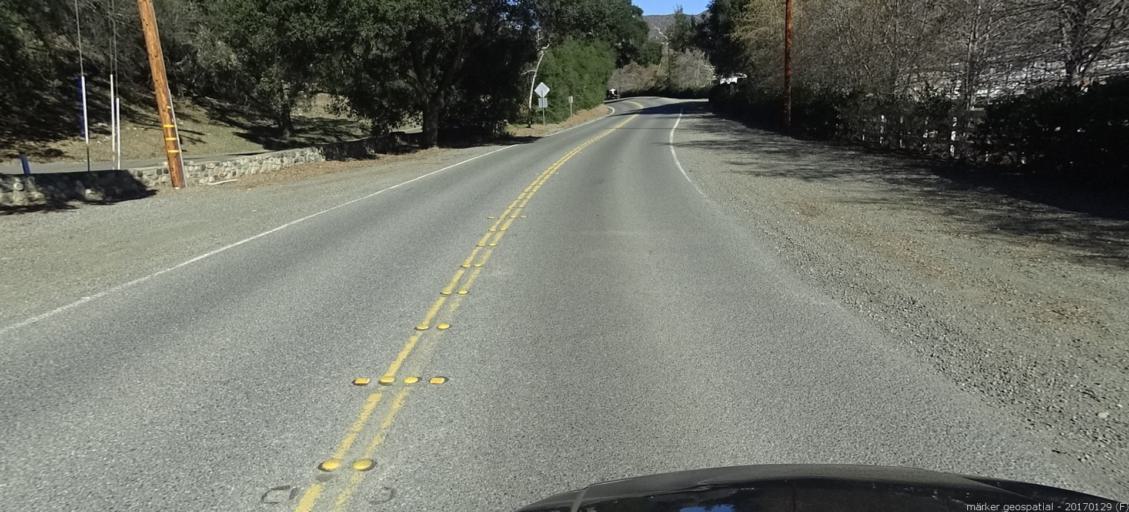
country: US
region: California
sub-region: Orange County
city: Rancho Santa Margarita
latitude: 33.6537
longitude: -117.6005
